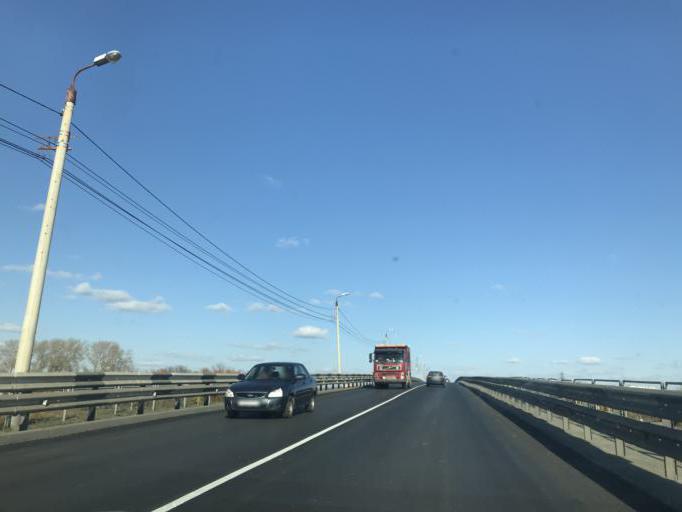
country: RU
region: Chelyabinsk
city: Roshchino
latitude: 55.2318
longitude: 61.2897
